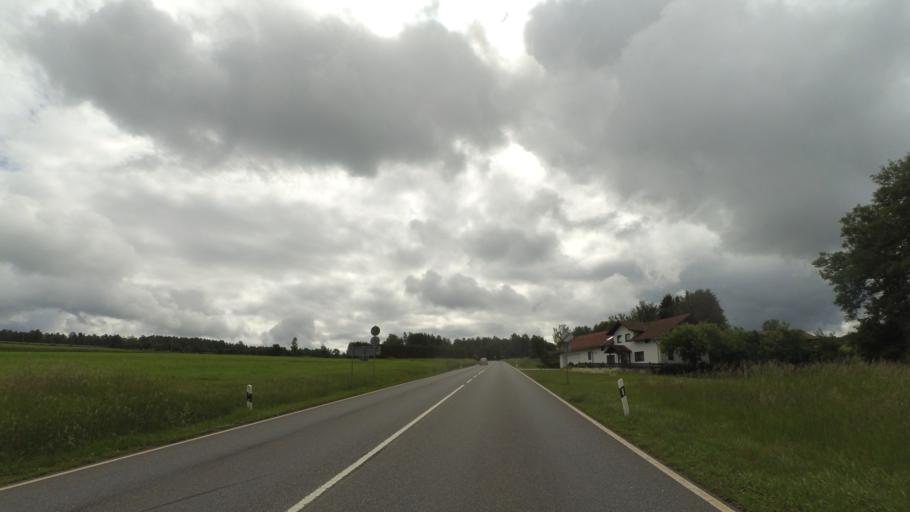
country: DE
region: Bavaria
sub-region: Lower Bavaria
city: Prackenbach
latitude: 49.0894
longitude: 12.8388
